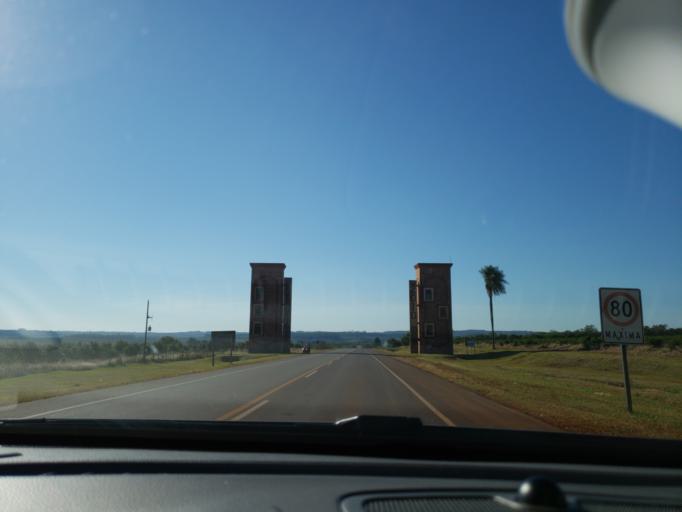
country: AR
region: Misiones
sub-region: Departamento de Apostoles
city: Apostoles
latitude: -27.8639
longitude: -55.7648
